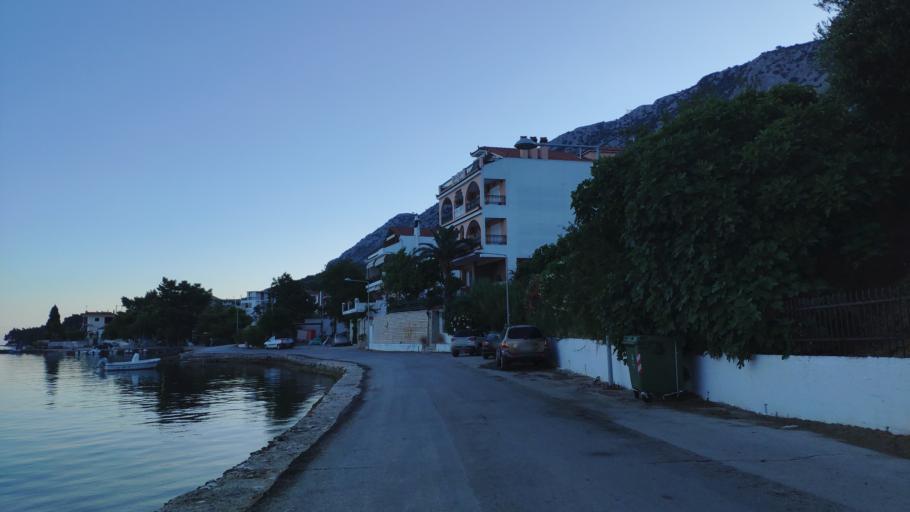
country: GR
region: West Greece
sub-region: Nomos Aitolias kai Akarnanias
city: Astakos
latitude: 38.5310
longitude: 21.0762
